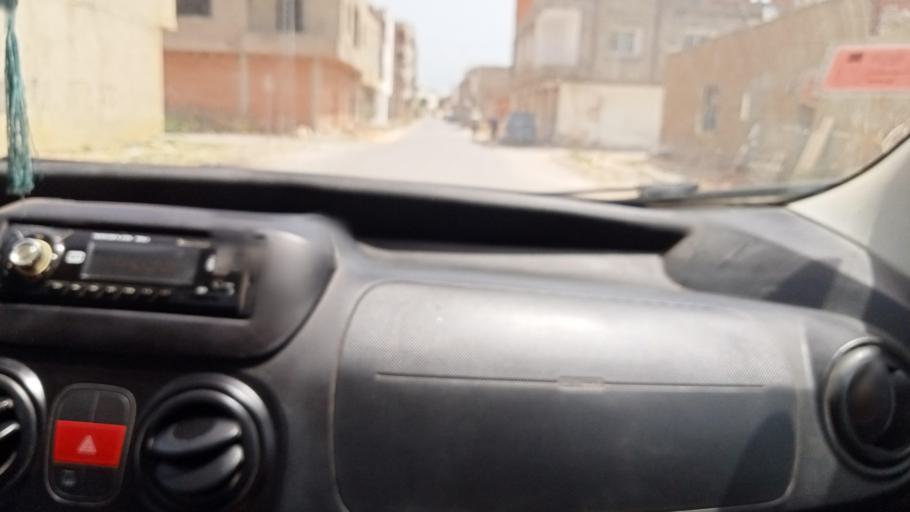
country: TN
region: Nabul
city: Qulaybiyah
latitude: 36.8582
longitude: 11.0879
